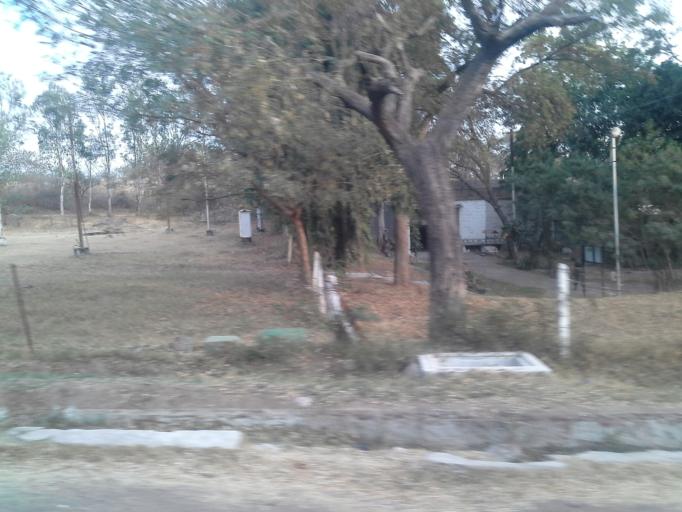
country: IN
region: Telangana
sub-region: Hyderabad
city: Hyderabad
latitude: 17.3778
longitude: 78.3978
